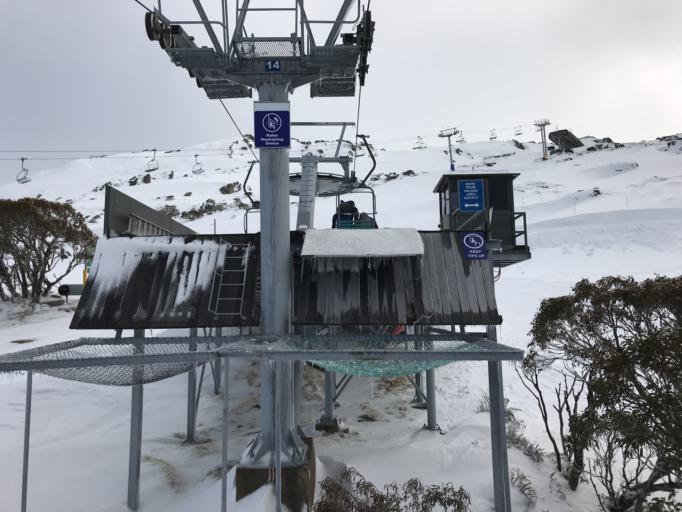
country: AU
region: New South Wales
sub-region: Snowy River
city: Jindabyne
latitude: -36.4008
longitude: 148.3960
